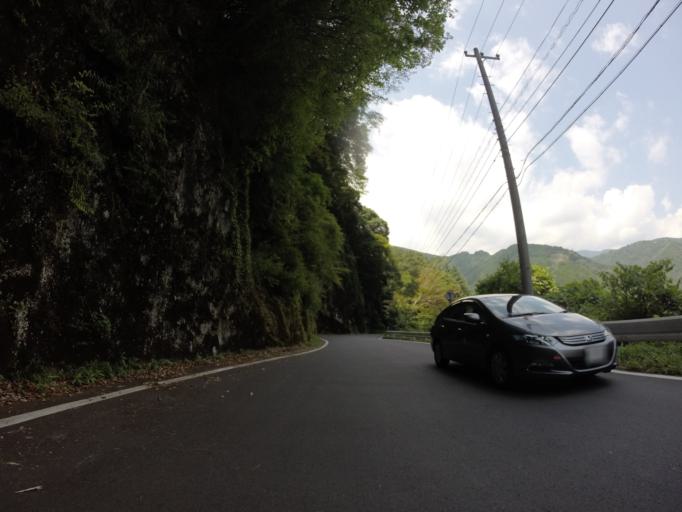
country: JP
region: Shizuoka
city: Shizuoka-shi
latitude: 35.2305
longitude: 138.3472
